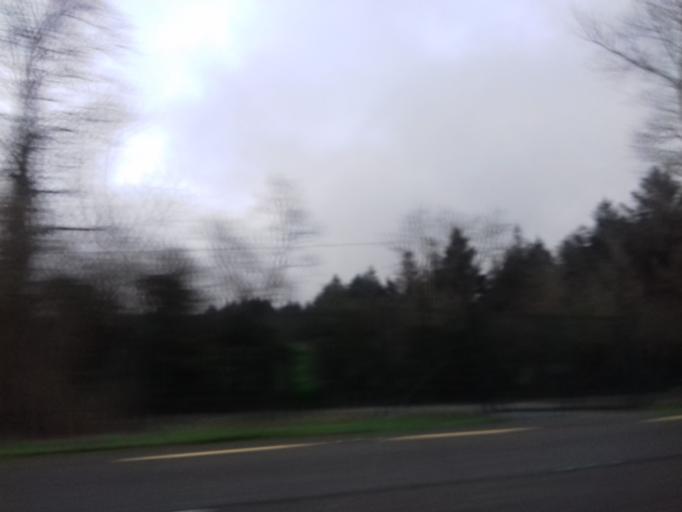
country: IE
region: Munster
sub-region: Ciarrai
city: Castleisland
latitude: 52.2659
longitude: -9.4420
